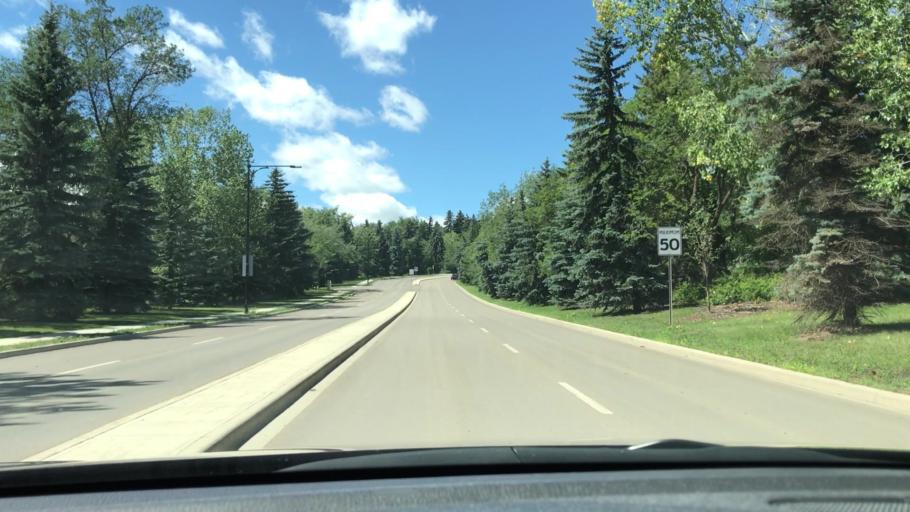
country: CA
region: Alberta
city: Edmonton
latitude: 53.5129
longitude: -113.5524
